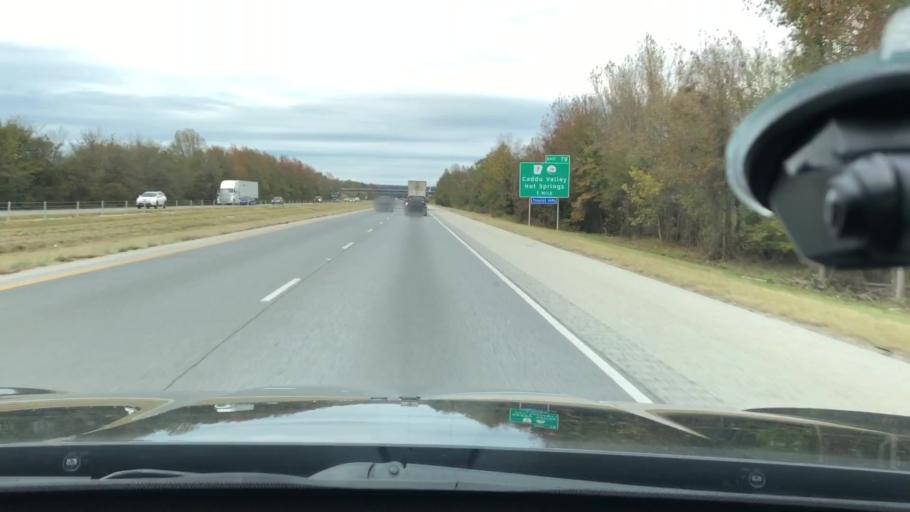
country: US
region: Arkansas
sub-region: Clark County
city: Arkadelphia
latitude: 34.1674
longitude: -93.0755
